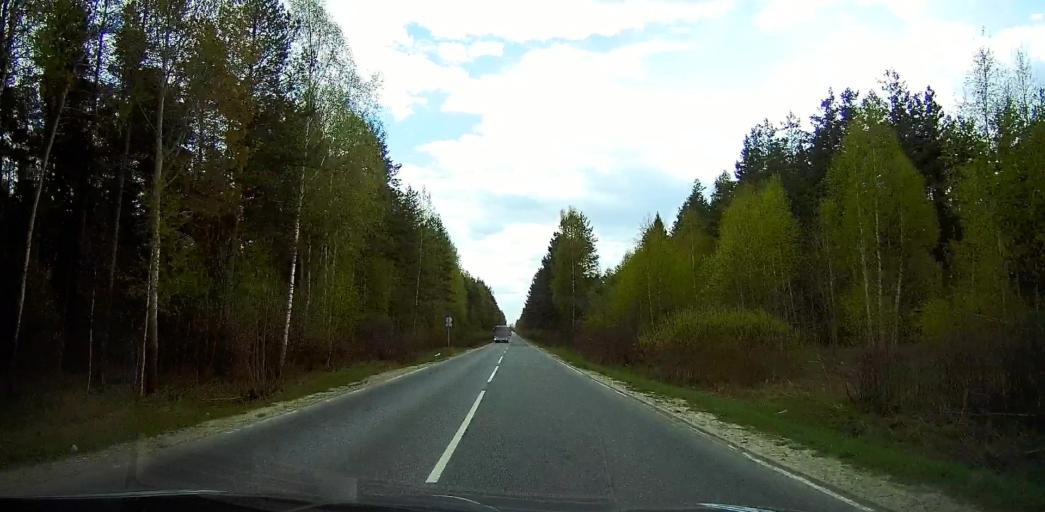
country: RU
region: Moskovskaya
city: Davydovo
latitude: 55.6568
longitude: 38.7543
